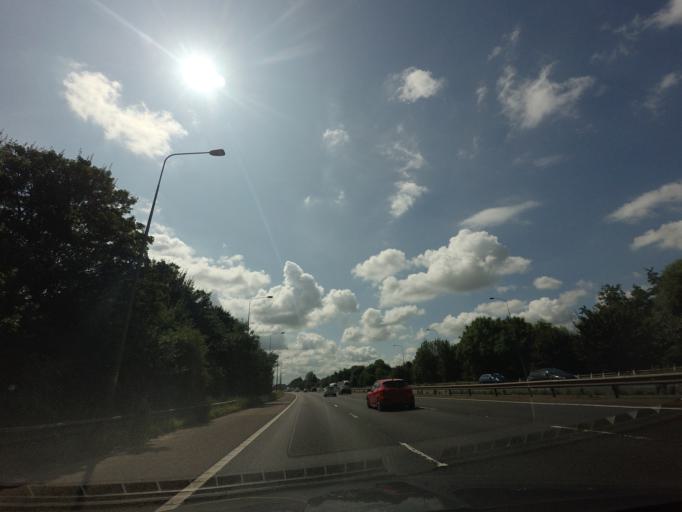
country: GB
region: England
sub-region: Lancashire
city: Clayton-le-Woods
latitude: 53.7038
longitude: -2.6769
